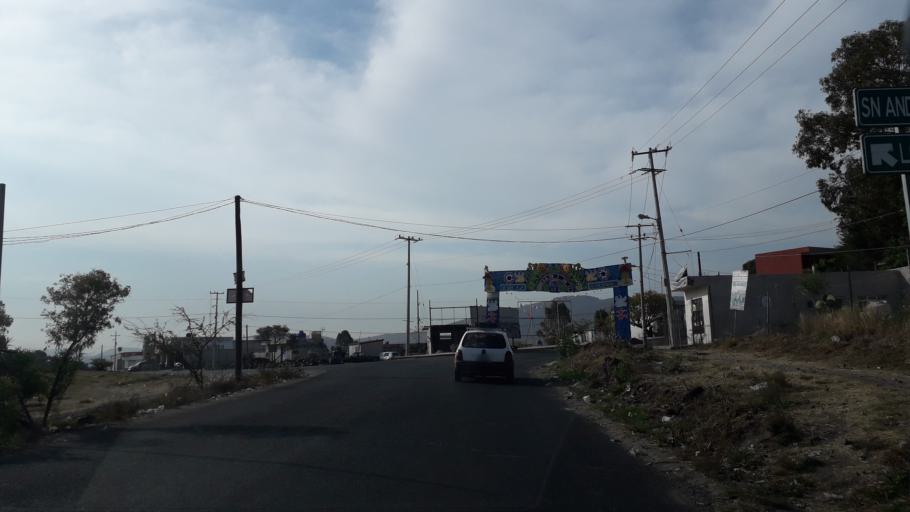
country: MX
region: Puebla
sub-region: Puebla
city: San Andres Azumiatla
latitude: 18.9111
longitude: -98.2417
